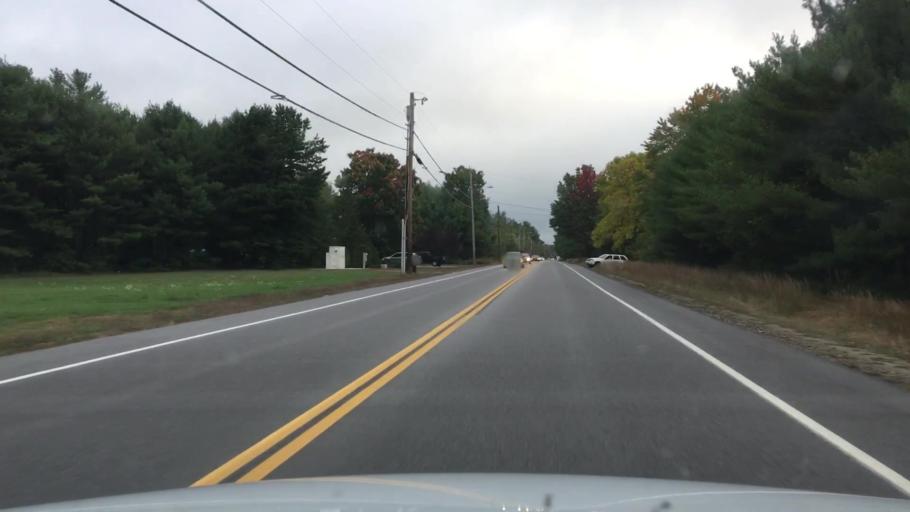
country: US
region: Maine
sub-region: Cumberland County
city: New Gloucester
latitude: 43.9344
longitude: -70.3519
